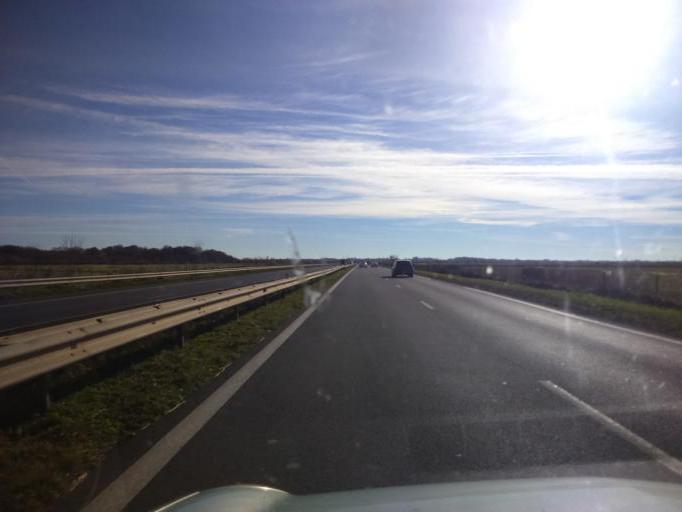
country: FR
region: Poitou-Charentes
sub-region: Departement de la Charente-Maritime
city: Saint-Laurent-de-la-Pree
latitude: 45.9834
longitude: -1.0207
